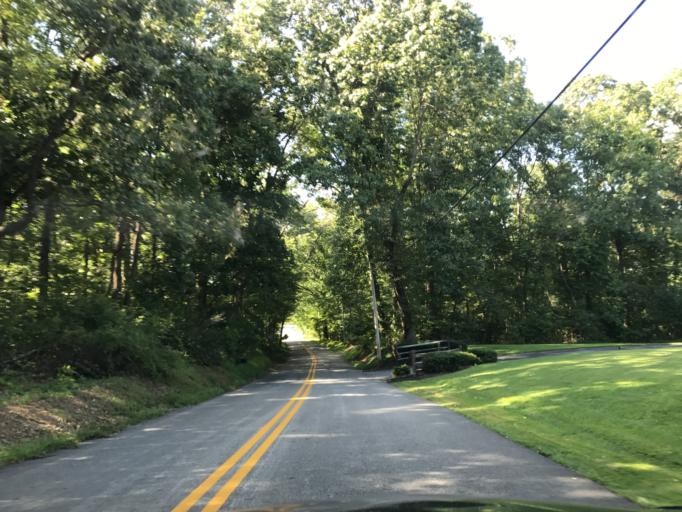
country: US
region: Pennsylvania
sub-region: York County
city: Stewartstown
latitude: 39.6990
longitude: -76.5845
